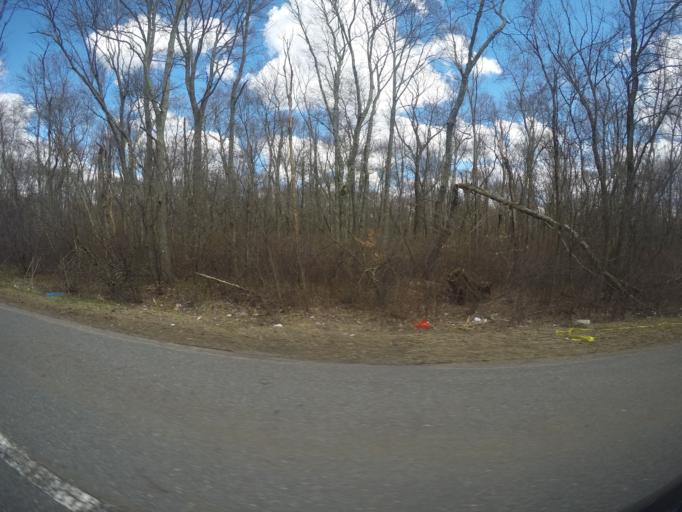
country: US
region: Massachusetts
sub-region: Bristol County
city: Raynham
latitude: 41.9910
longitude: -71.0693
